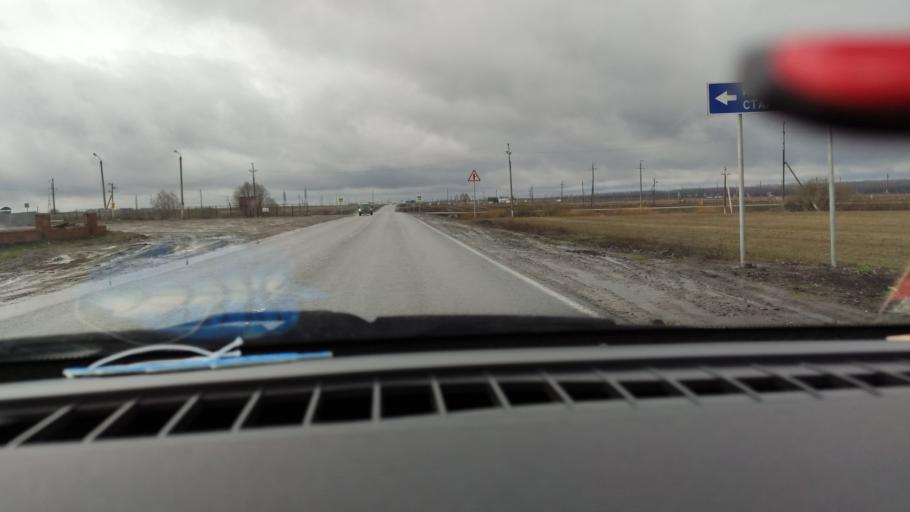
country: RU
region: Tatarstan
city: Nurlat
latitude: 54.4846
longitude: 50.8477
